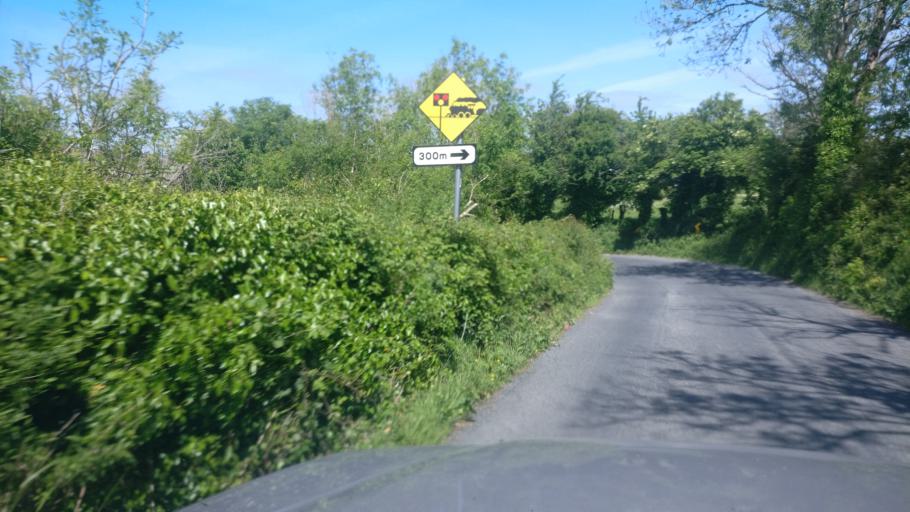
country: IE
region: Connaught
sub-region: County Galway
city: Gort
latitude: 53.0912
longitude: -8.8056
